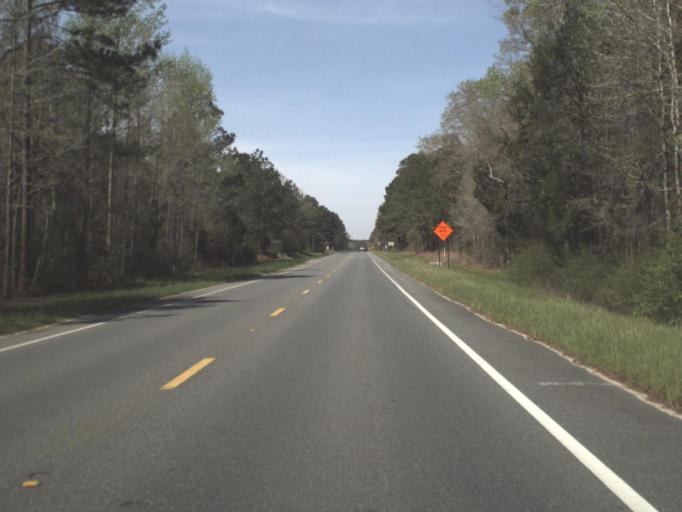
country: US
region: Florida
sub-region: Holmes County
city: Bonifay
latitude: 30.7793
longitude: -85.6284
